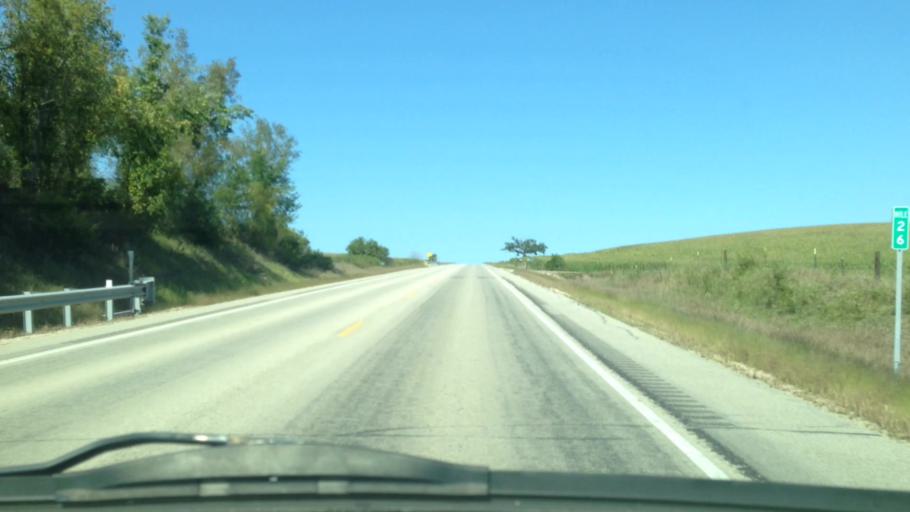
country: US
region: Minnesota
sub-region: Fillmore County
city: Rushford
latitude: 43.8513
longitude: -91.7490
